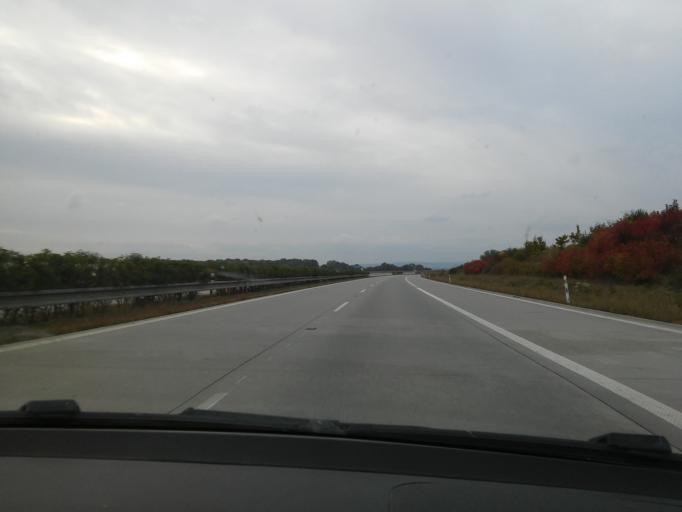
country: CZ
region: Olomoucky
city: Kojetin
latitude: 49.3208
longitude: 17.2579
